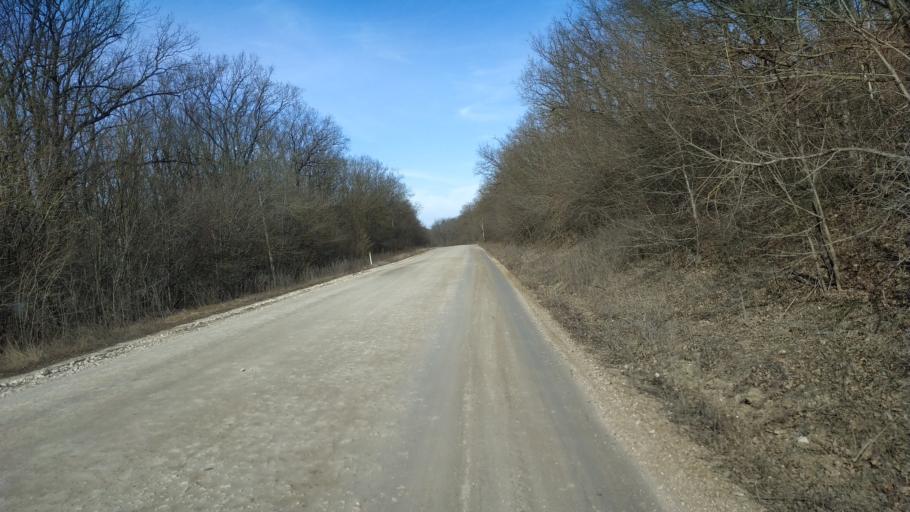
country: MD
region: Straseni
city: Straseni
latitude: 47.0366
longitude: 28.6140
